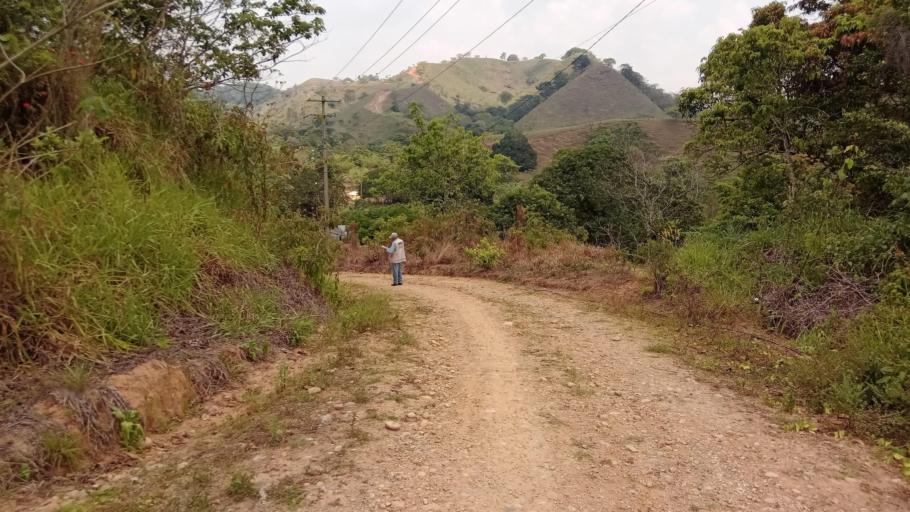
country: MX
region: Tabasco
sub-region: Huimanguillo
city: Francisco Rueda
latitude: 17.5895
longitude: -93.8581
